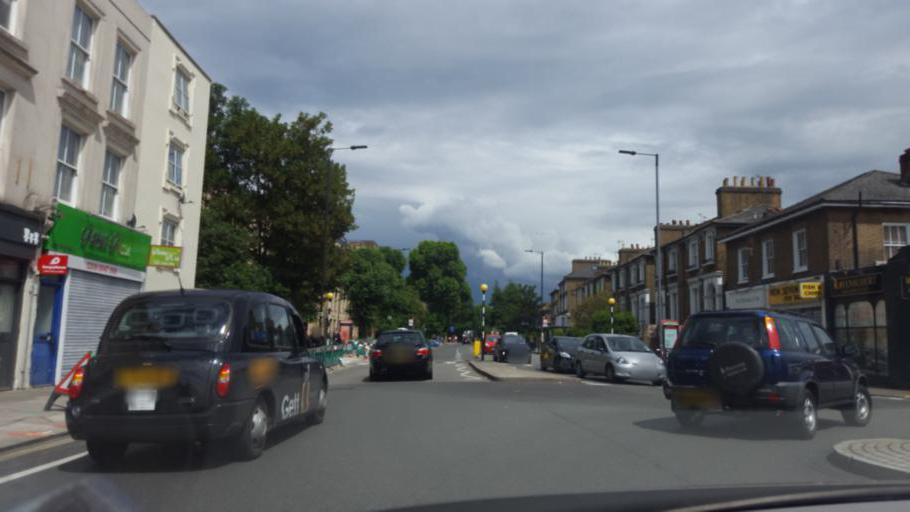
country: GB
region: England
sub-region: Greater London
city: Hammersmith
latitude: 51.5000
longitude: -0.2392
